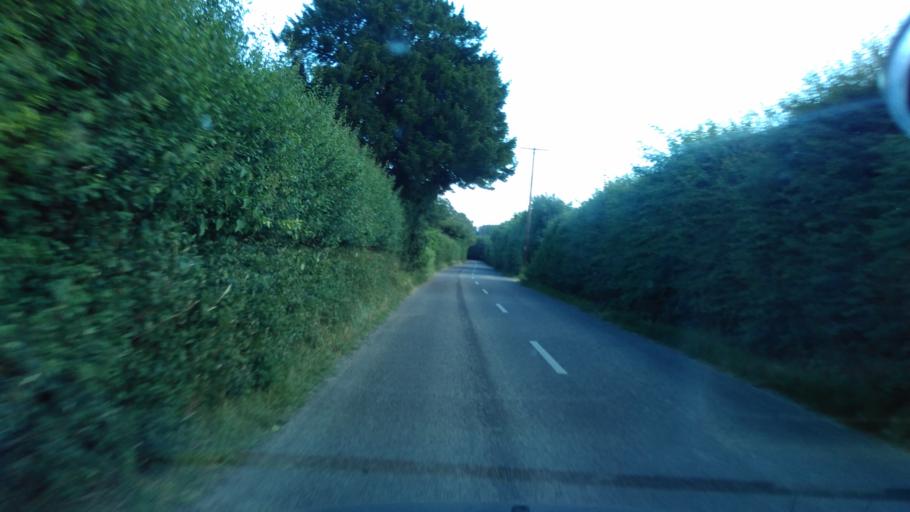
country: GB
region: England
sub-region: Kent
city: Dunkirk
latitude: 51.2552
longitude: 0.9569
